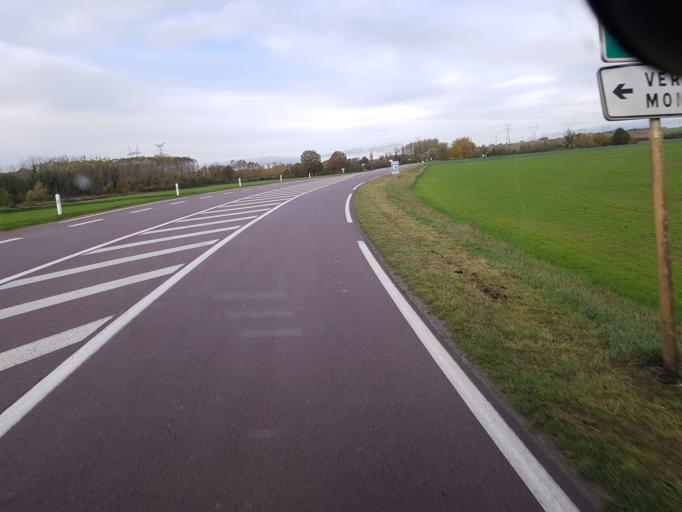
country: FR
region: Champagne-Ardenne
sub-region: Departement de l'Aube
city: Lusigny-sur-Barse
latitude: 48.2625
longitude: 4.2227
